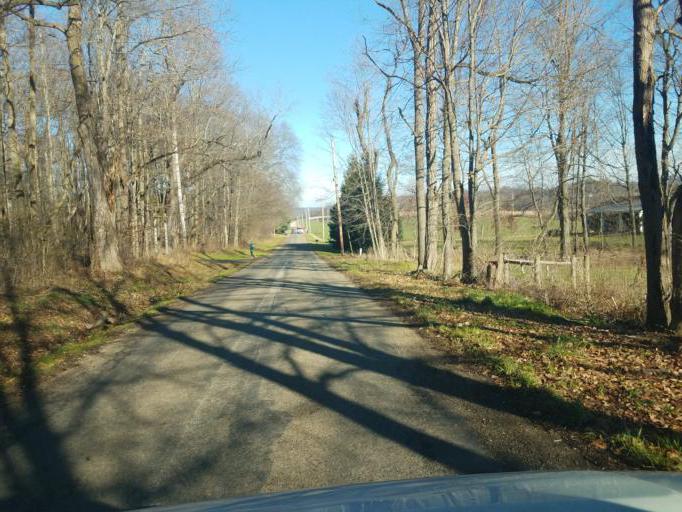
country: US
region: Ohio
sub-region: Richland County
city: Lincoln Heights
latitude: 40.7174
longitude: -82.4464
